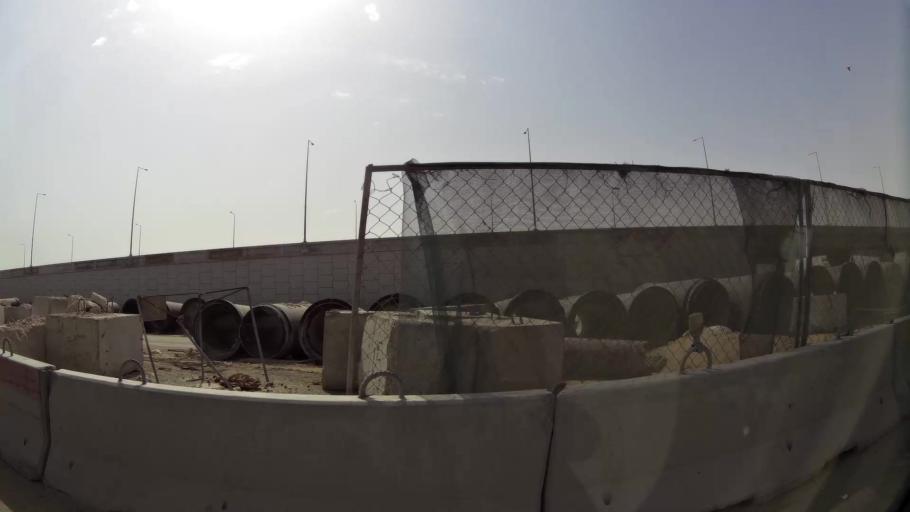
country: QA
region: Al Wakrah
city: Al Wukayr
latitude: 25.1936
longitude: 51.4560
